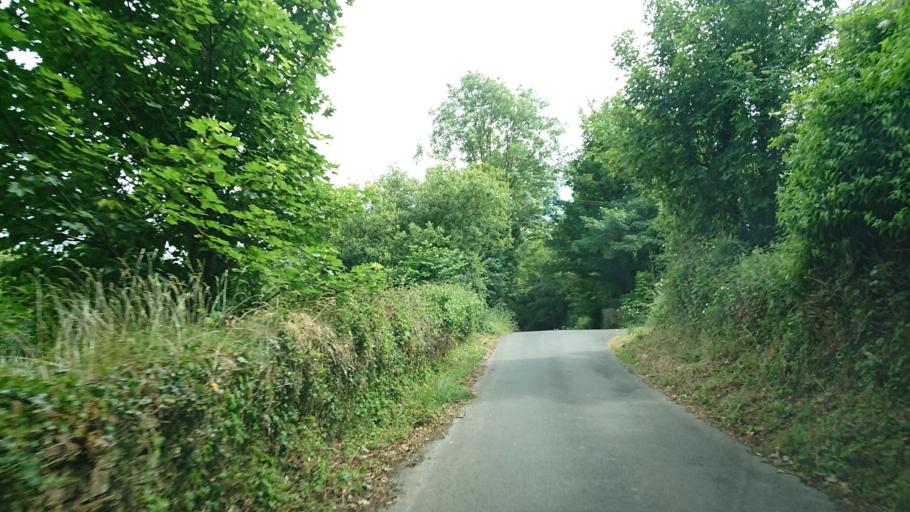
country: IE
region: Munster
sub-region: Waterford
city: Waterford
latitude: 52.2743
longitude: -7.1479
